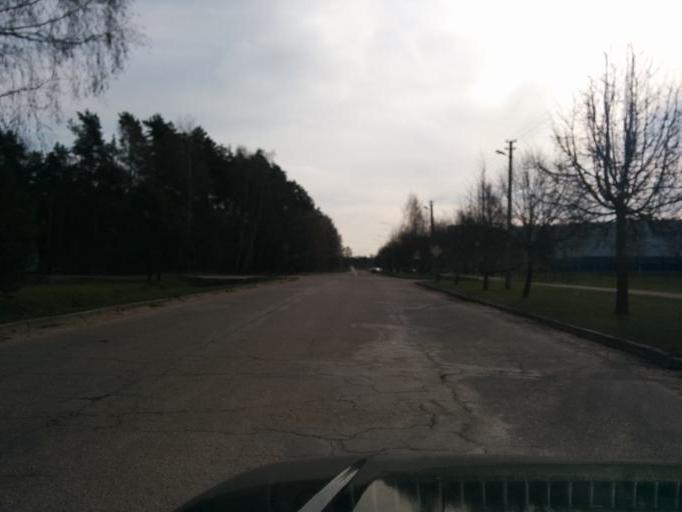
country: LV
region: Jelgava
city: Jelgava
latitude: 56.6709
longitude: 23.7474
